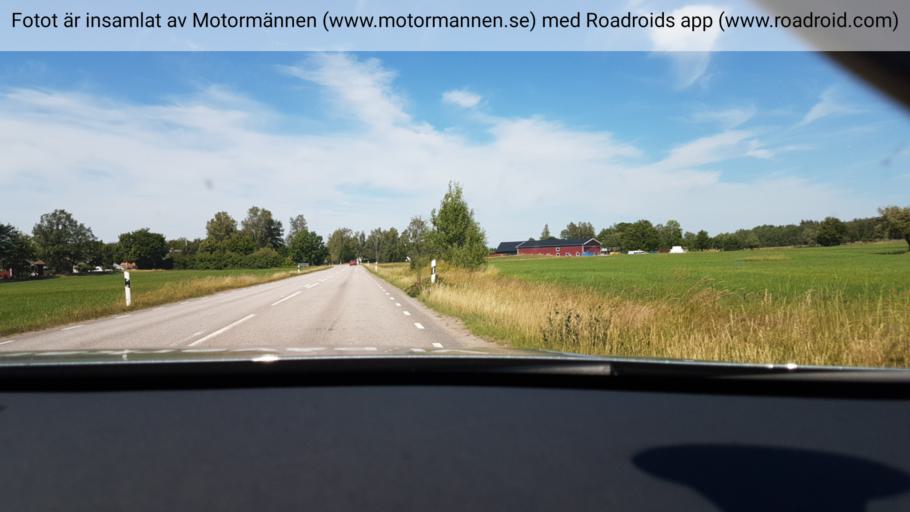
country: SE
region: Vaestra Goetaland
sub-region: Skovde Kommun
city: Stopen
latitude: 58.5068
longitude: 13.9716
